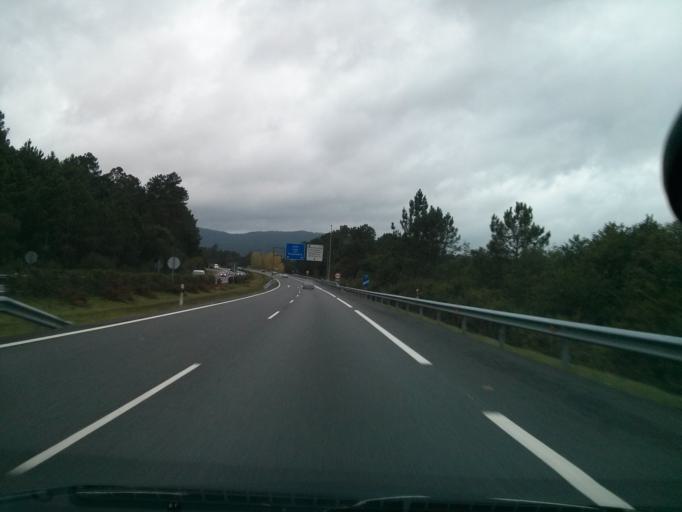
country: ES
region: Galicia
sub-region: Provincia de Pontevedra
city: Ponteareas
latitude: 42.1557
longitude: -8.4946
